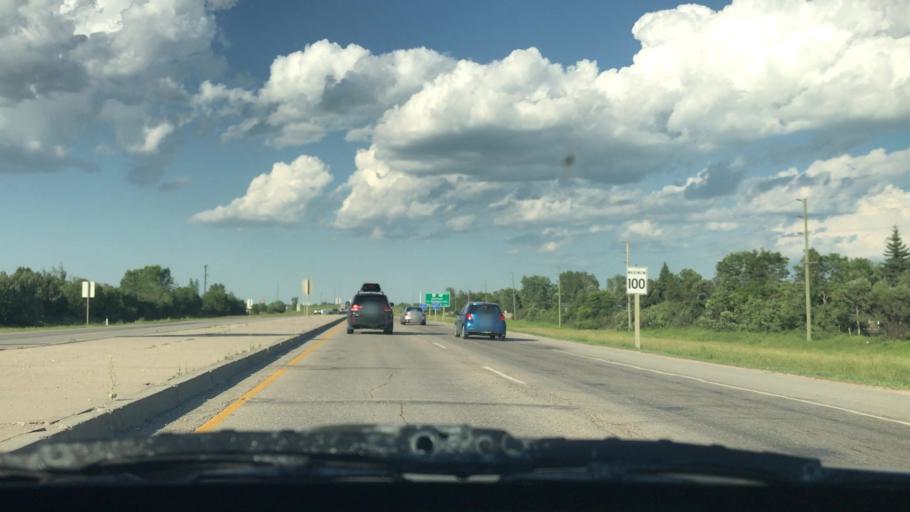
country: CA
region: Manitoba
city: Winnipeg
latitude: 49.7717
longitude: -97.1715
